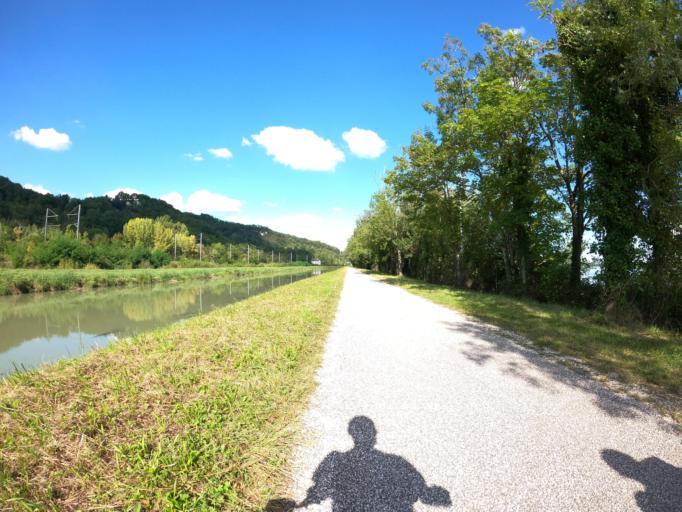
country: FR
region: Midi-Pyrenees
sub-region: Departement du Tarn-et-Garonne
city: Saint-Nicolas-de-la-Grave
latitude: 44.0876
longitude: 0.9893
